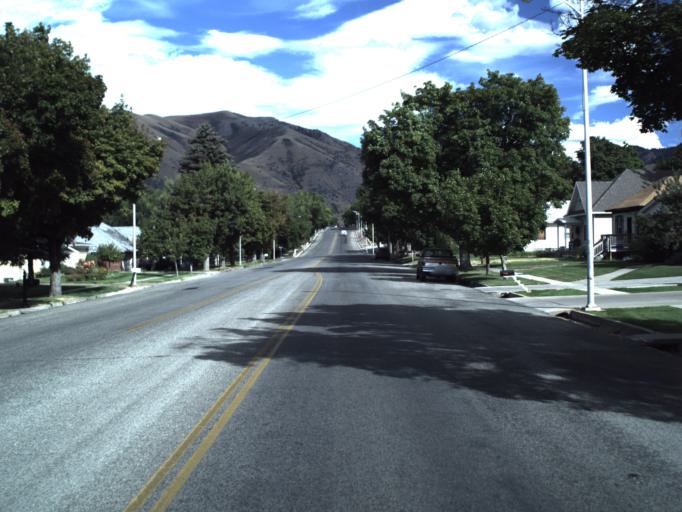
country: US
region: Utah
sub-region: Cache County
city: Hyrum
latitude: 41.6340
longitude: -111.8519
